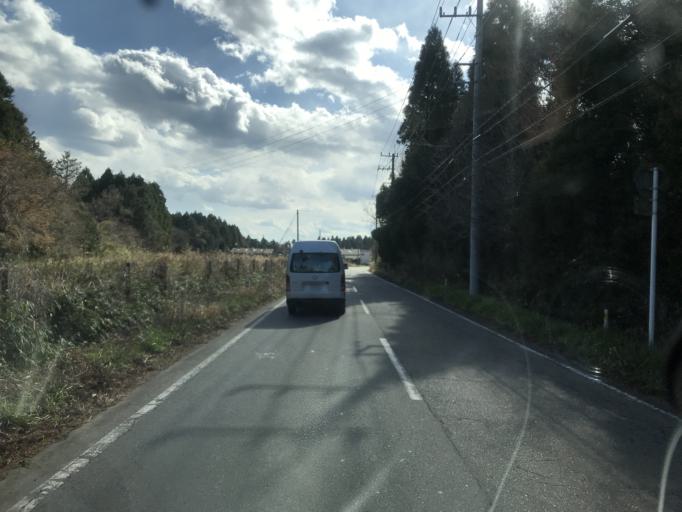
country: JP
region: Chiba
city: Sawara
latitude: 35.8645
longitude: 140.4163
